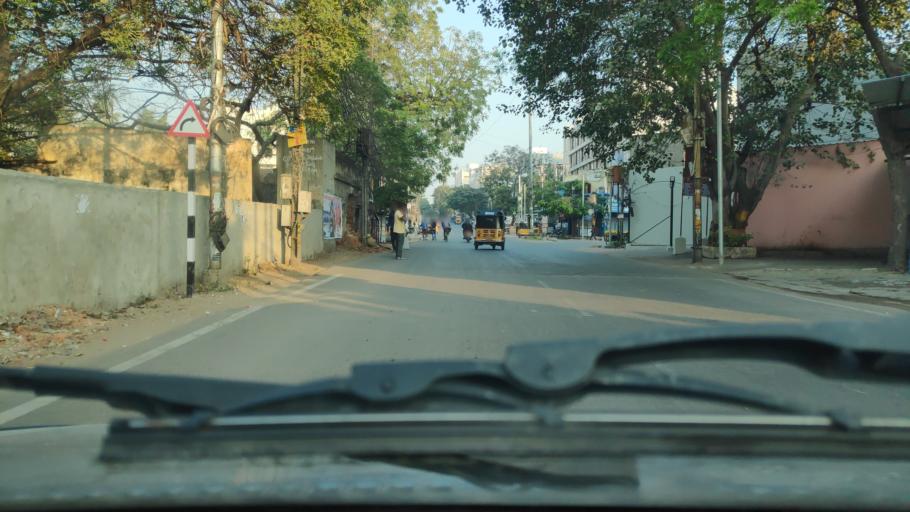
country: IN
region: Telangana
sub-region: Rangareddi
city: Gaddi Annaram
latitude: 17.3660
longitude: 78.5211
